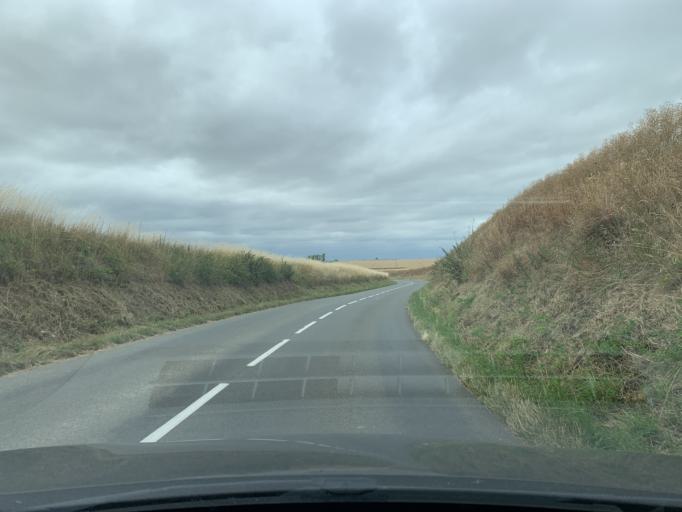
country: FR
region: Nord-Pas-de-Calais
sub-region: Departement du Nord
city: Fechain
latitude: 50.2390
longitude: 3.2075
